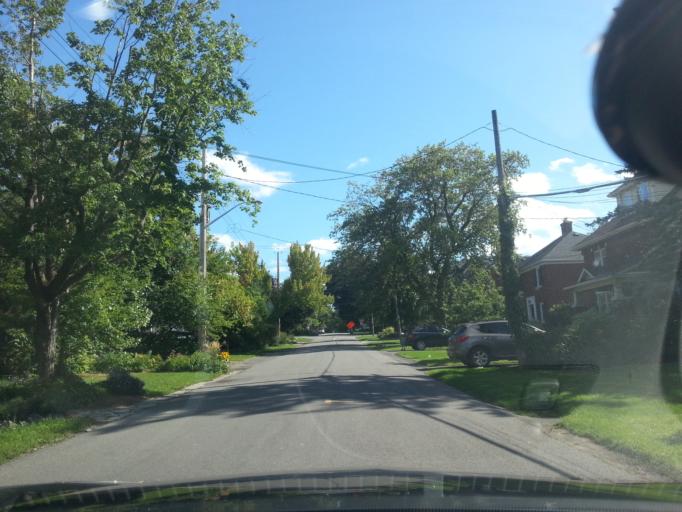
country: CA
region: Ontario
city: Ottawa
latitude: 45.3882
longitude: -75.7575
